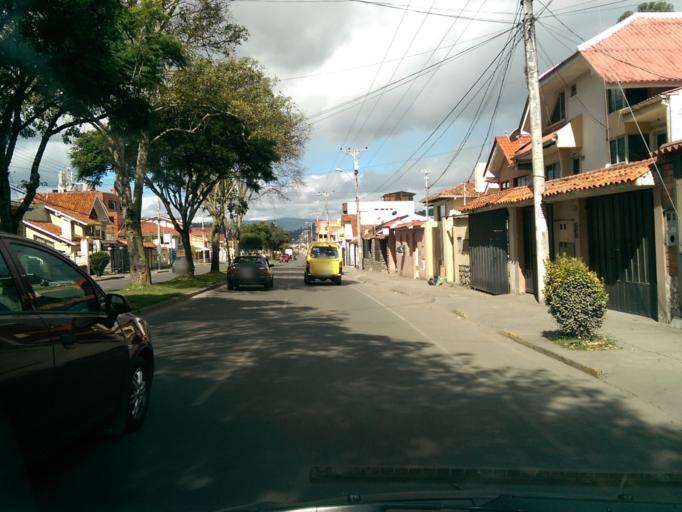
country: EC
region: Azuay
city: Cuenca
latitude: -2.9069
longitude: -79.0222
